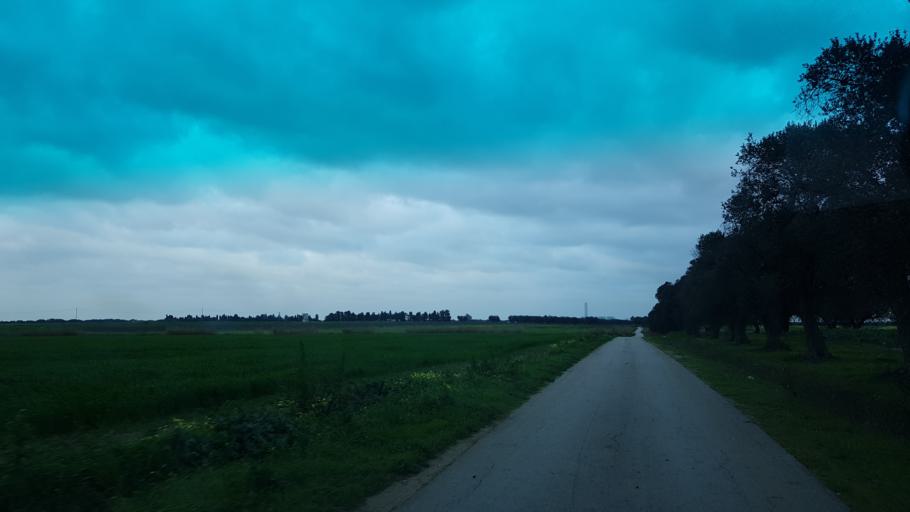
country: IT
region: Apulia
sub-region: Provincia di Brindisi
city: La Rosa
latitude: 40.5957
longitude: 17.9728
